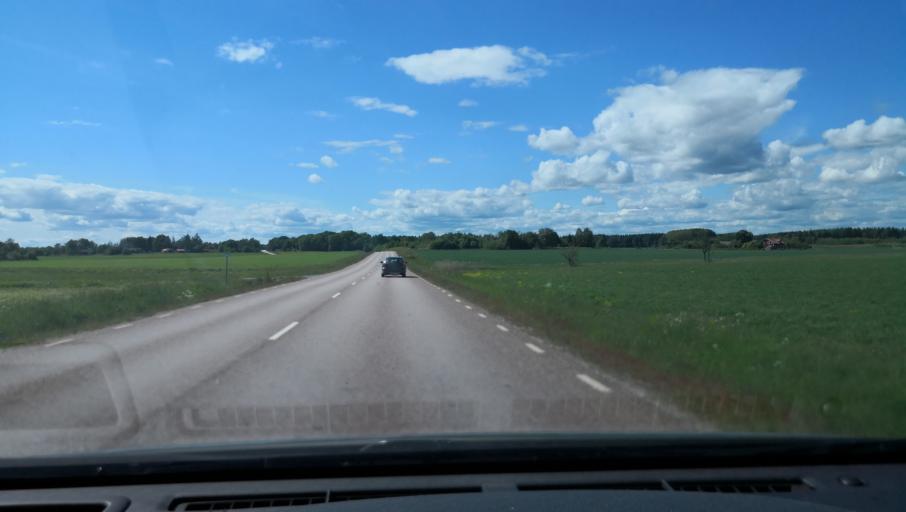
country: SE
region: Vaestmanland
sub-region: Kungsors Kommun
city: Kungsoer
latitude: 59.2888
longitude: 16.1009
